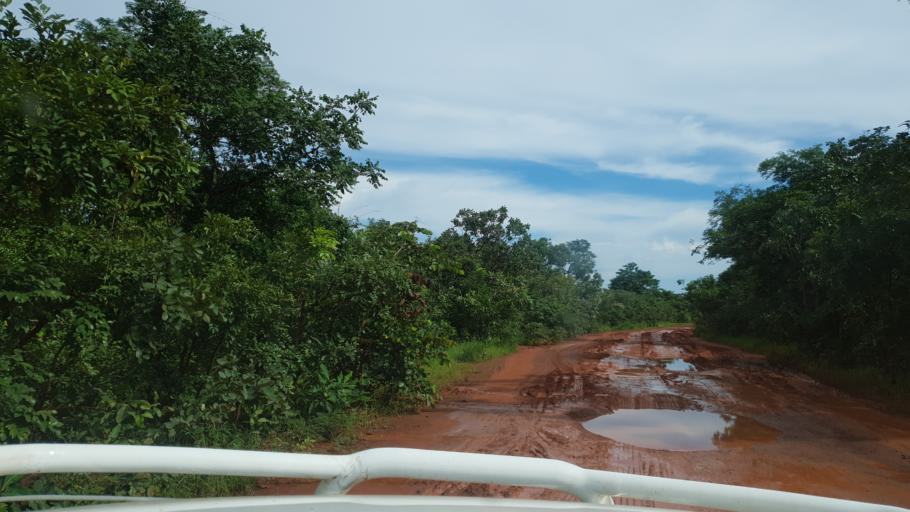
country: ML
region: Sikasso
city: Kolondieba
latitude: 10.7407
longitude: -6.9105
